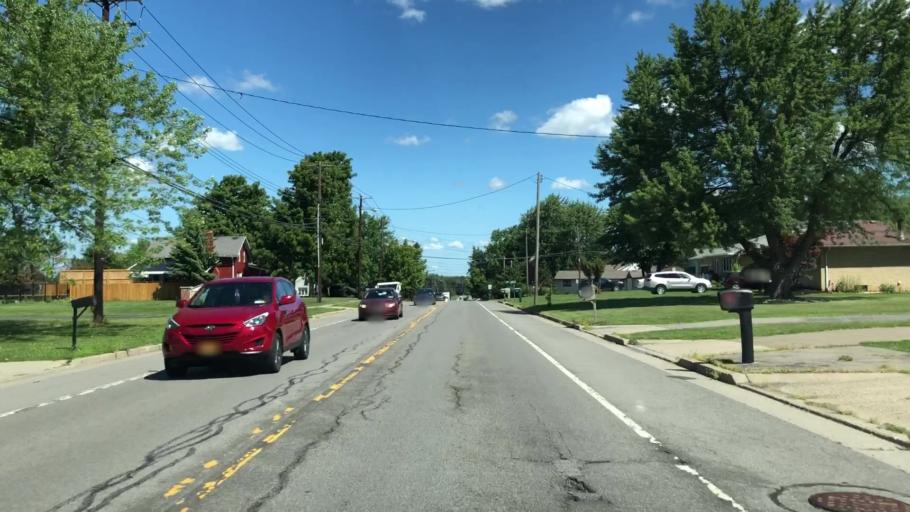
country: US
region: New York
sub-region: Erie County
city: Depew
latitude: 42.8769
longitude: -78.7090
